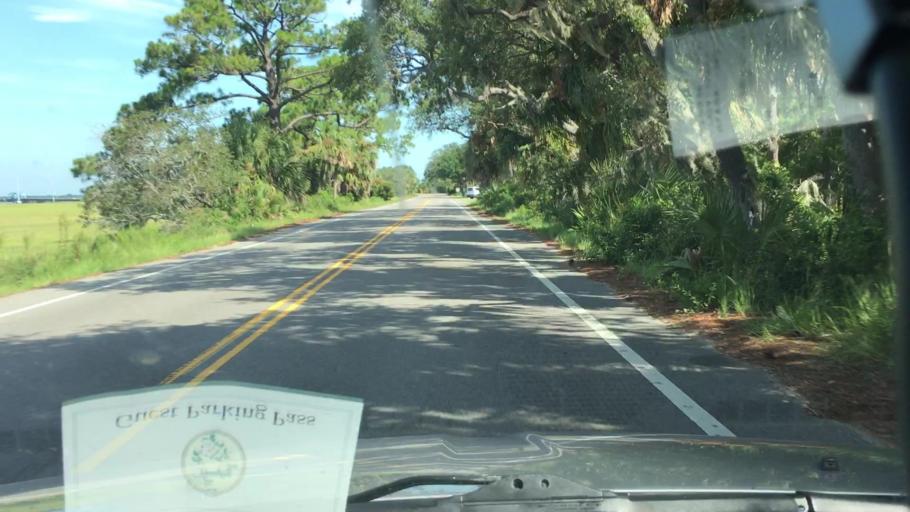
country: US
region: South Carolina
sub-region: Beaufort County
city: Beaufort
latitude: 32.3978
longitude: -80.4427
